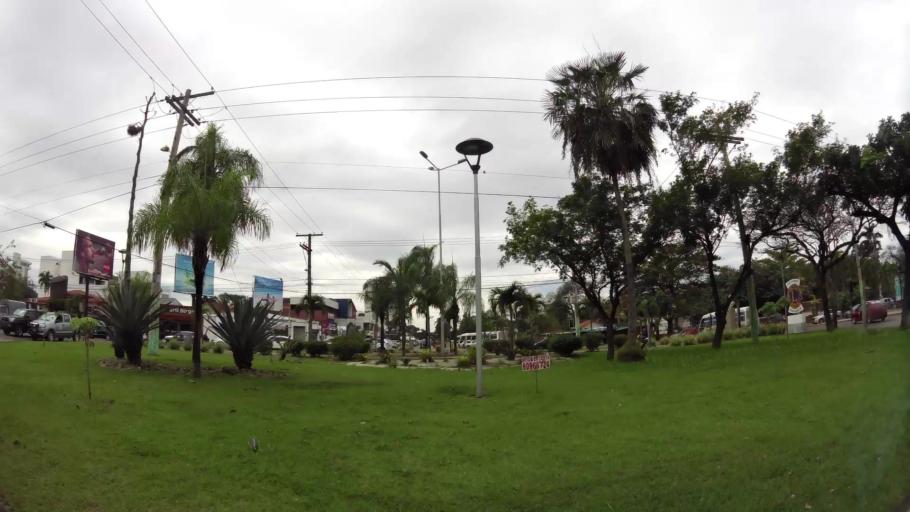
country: BO
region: Santa Cruz
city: Santa Cruz de la Sierra
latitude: -17.7635
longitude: -63.1969
